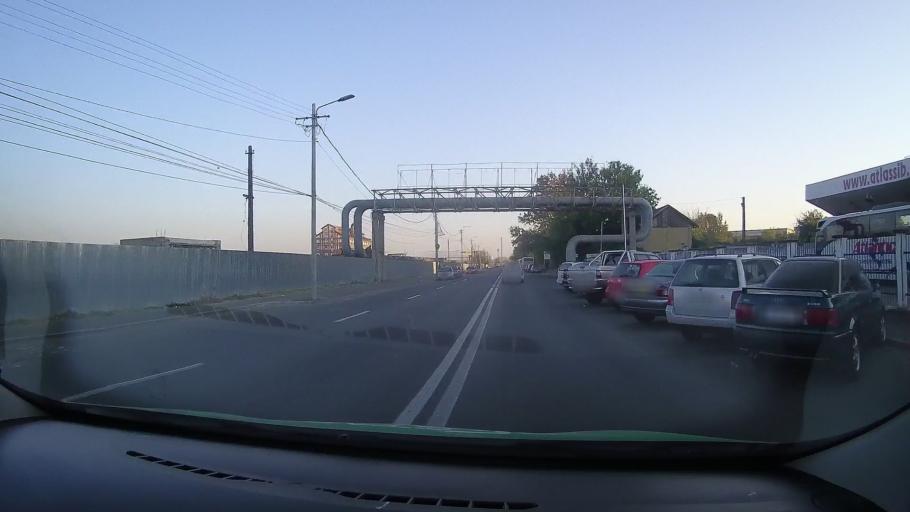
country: RO
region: Arad
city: Arad
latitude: 46.1914
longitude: 21.3194
